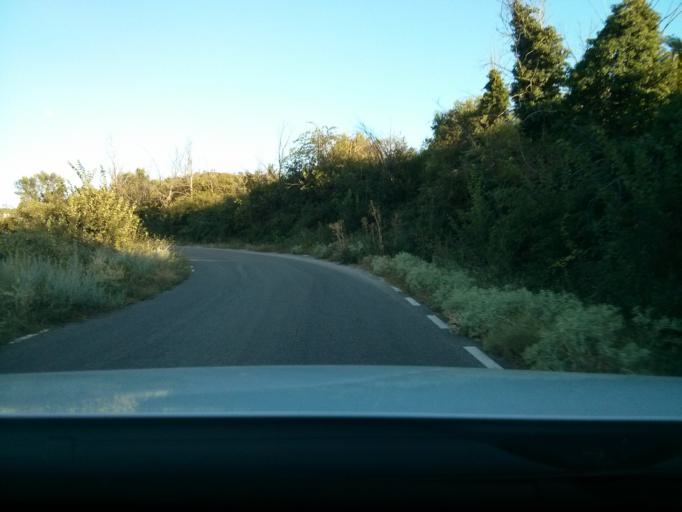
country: ES
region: Castille-La Mancha
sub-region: Provincia de Guadalajara
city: Mantiel
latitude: 40.6219
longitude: -2.6393
